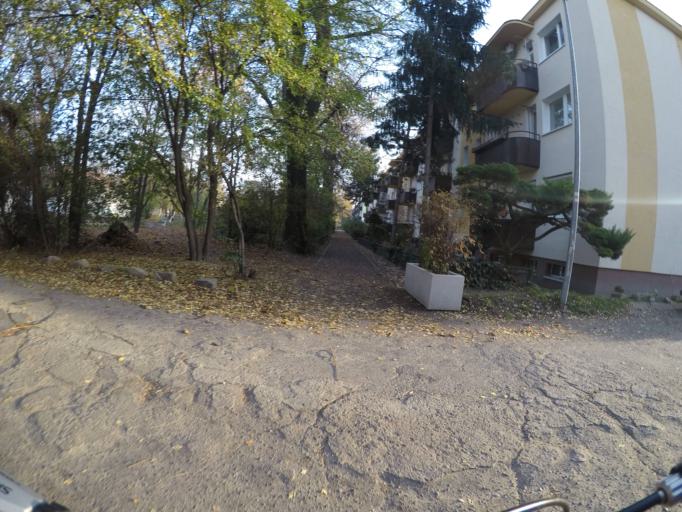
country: SK
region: Bratislavsky
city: Bratislava
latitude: 48.1753
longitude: 17.1575
